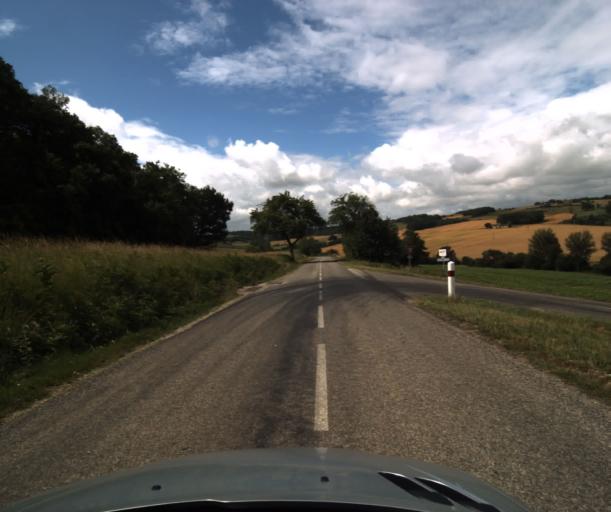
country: FR
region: Midi-Pyrenees
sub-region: Departement du Tarn-et-Garonne
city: Lavit
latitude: 43.9523
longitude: 0.9092
